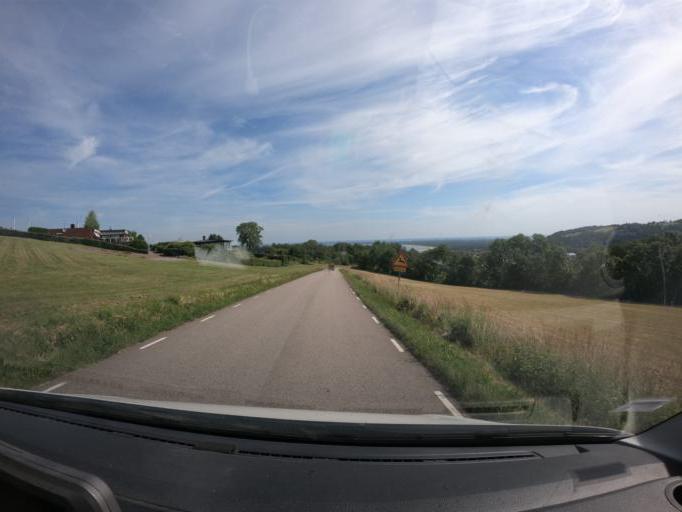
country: SE
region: Skane
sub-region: Bastads Kommun
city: Bastad
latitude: 56.4216
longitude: 12.8365
